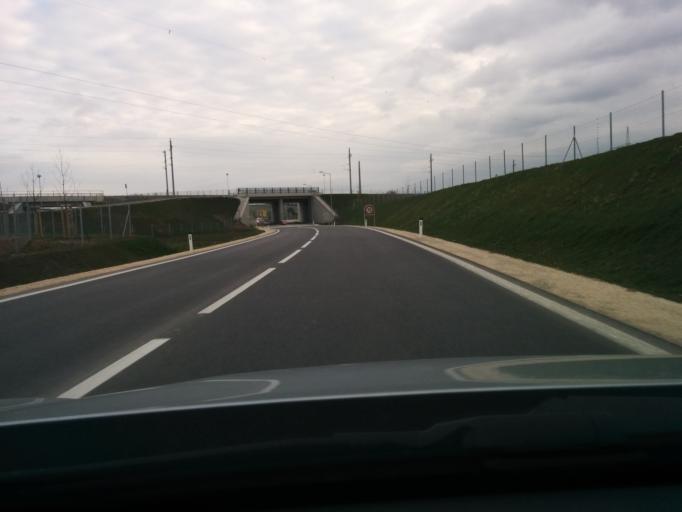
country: AT
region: Lower Austria
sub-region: Politischer Bezirk Mistelbach
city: Mistelbach
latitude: 48.5637
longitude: 16.5545
